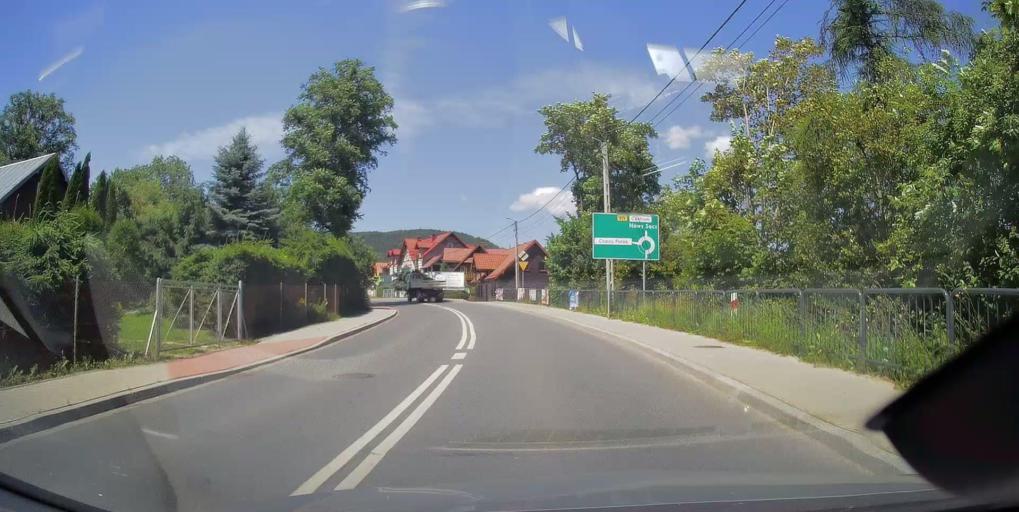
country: PL
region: Lesser Poland Voivodeship
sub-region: Powiat nowosadecki
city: Krynica-Zdroj
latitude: 49.3989
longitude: 20.9561
